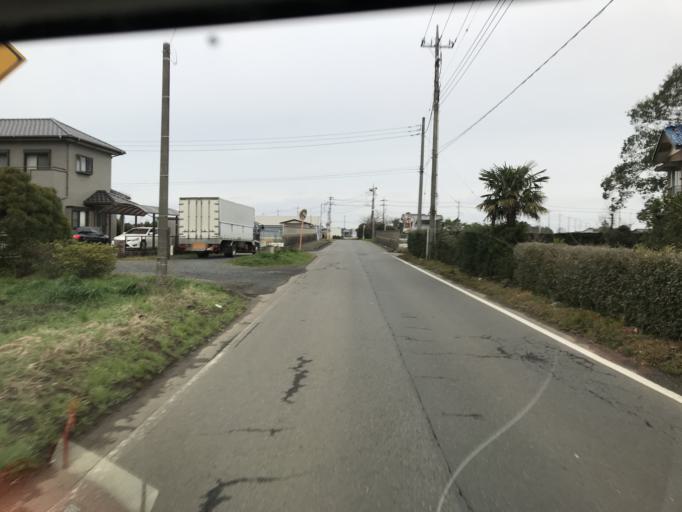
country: JP
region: Chiba
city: Sawara
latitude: 35.8505
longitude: 140.5125
